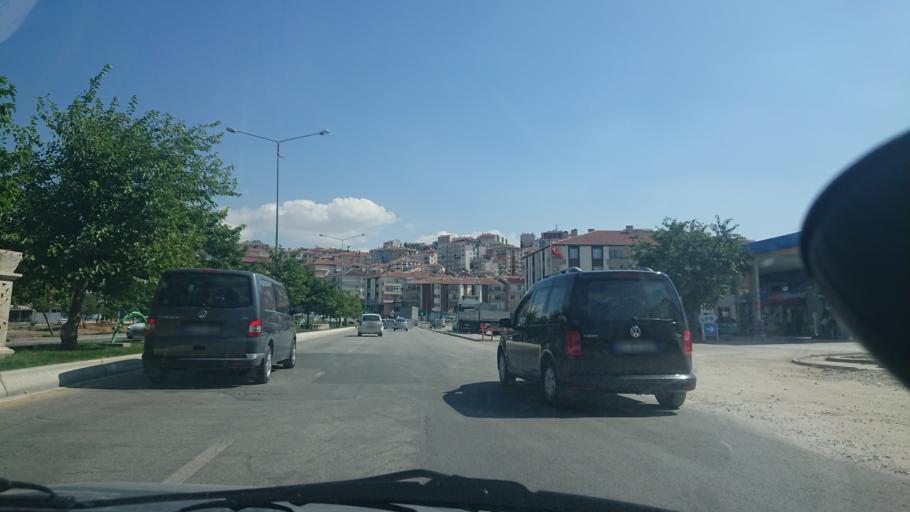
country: TR
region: Ankara
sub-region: Goelbasi
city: Golbasi
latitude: 39.8010
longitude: 32.8109
